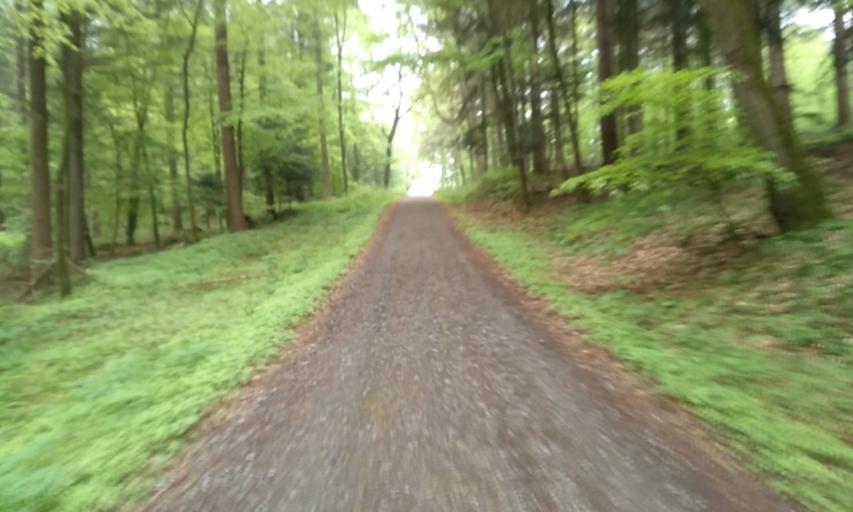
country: DE
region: Lower Saxony
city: Nottensdorf
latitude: 53.4758
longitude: 9.6301
